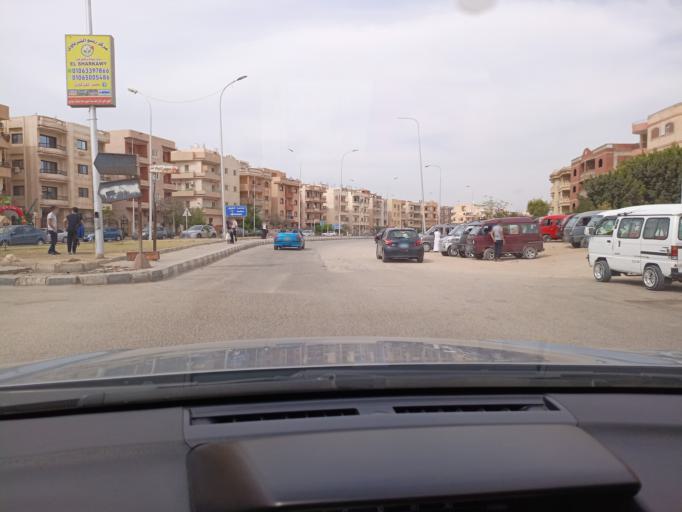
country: EG
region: Muhafazat al Qalyubiyah
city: Al Khankah
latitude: 30.2420
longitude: 31.4822
